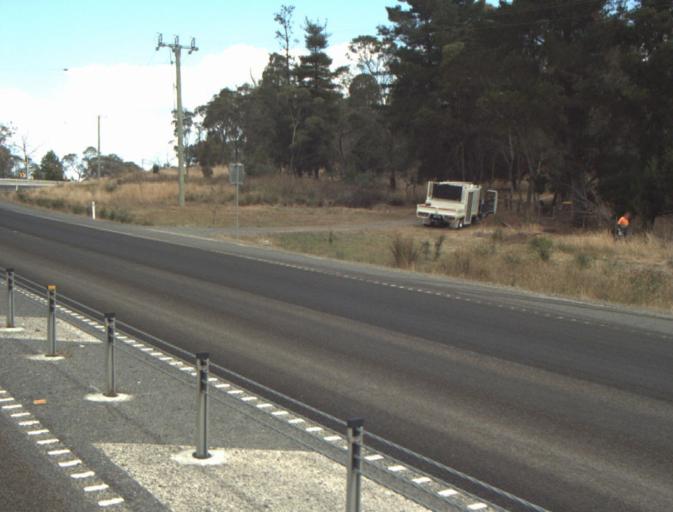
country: AU
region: Tasmania
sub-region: Launceston
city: Mayfield
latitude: -41.2959
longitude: 147.0492
